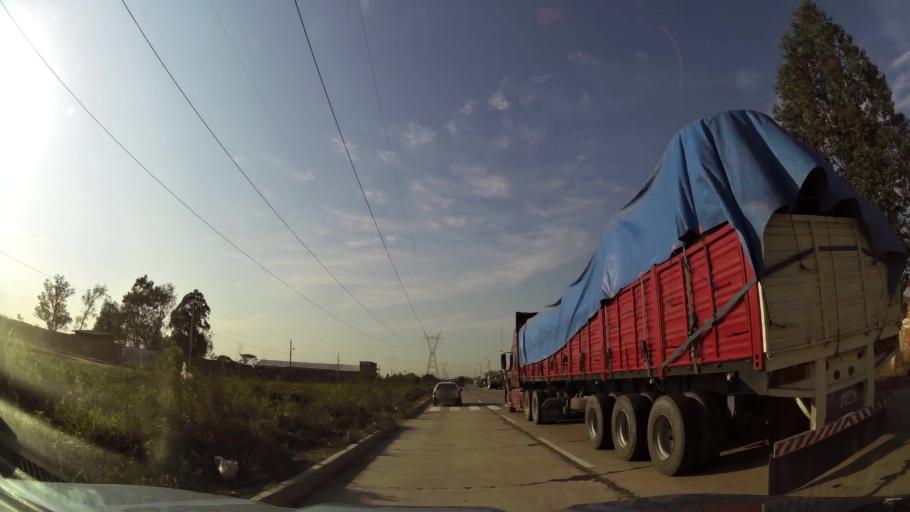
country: BO
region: Santa Cruz
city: Santa Cruz de la Sierra
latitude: -17.6945
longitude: -63.1386
